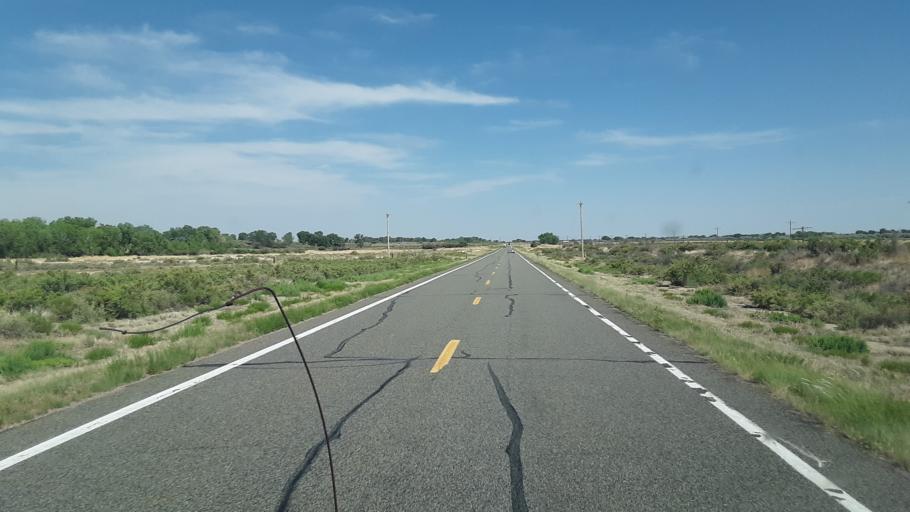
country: US
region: Colorado
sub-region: Otero County
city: Fowler
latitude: 38.2194
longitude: -104.1974
